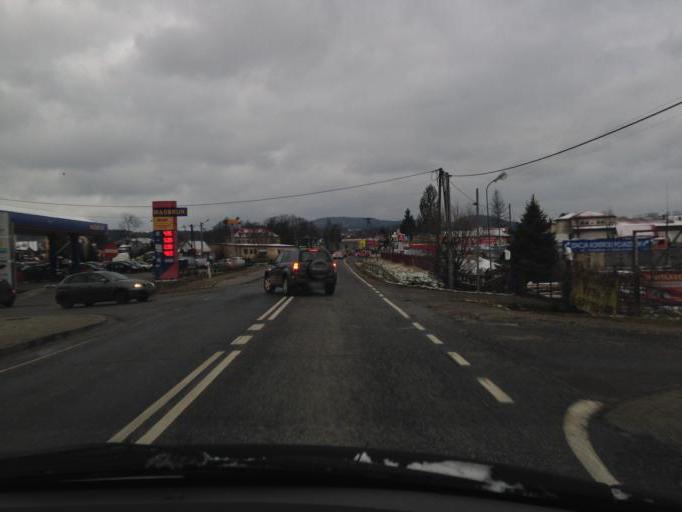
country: PL
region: Lesser Poland Voivodeship
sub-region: Powiat tarnowski
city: Zakliczyn
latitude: 49.8593
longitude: 20.8140
